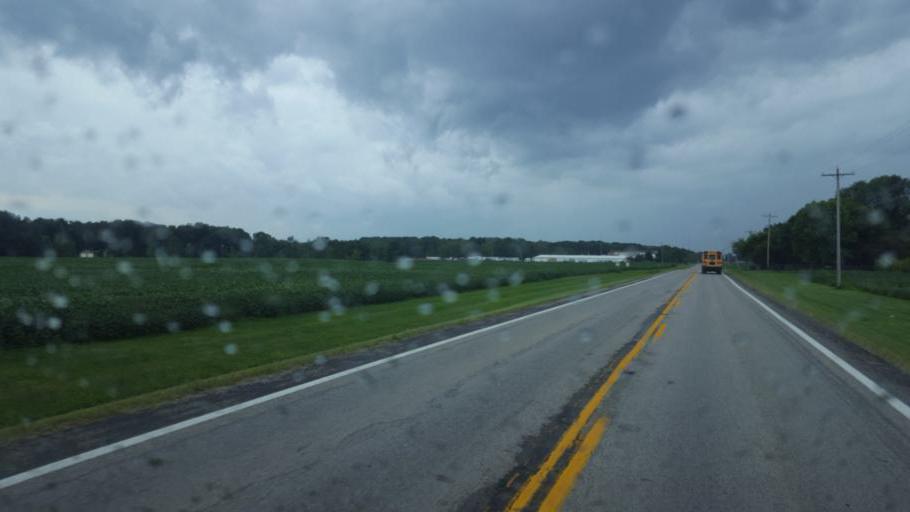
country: US
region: Ohio
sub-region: Delaware County
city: Delaware
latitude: 40.3164
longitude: -83.0329
